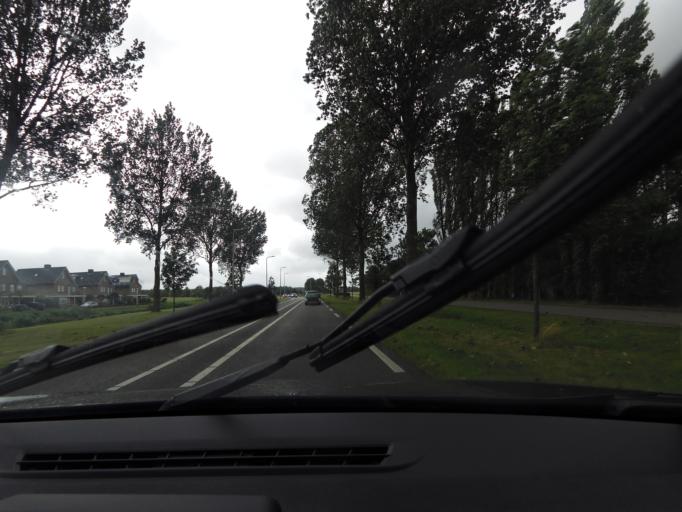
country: NL
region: South Holland
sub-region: Gemeente Hellevoetsluis
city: Nieuwenhoorn
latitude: 51.8508
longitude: 4.1640
